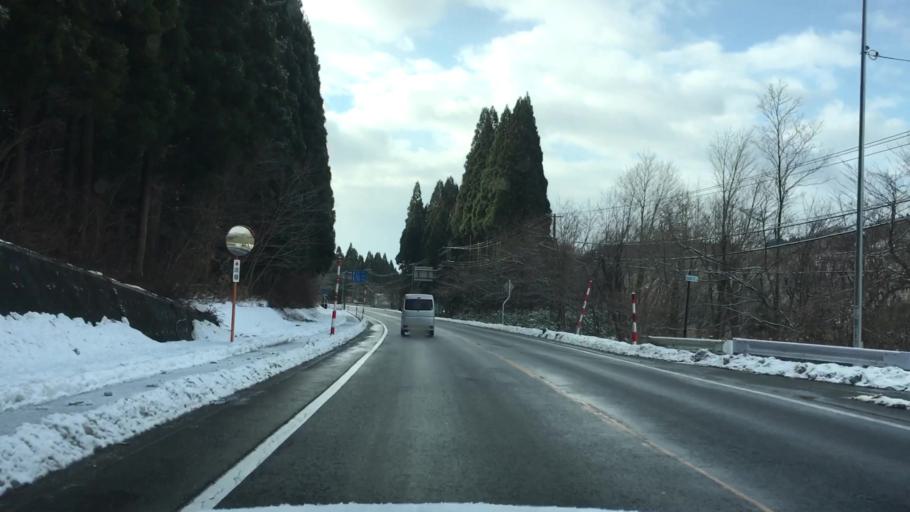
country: JP
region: Akita
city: Odate
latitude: 40.3855
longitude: 140.6039
